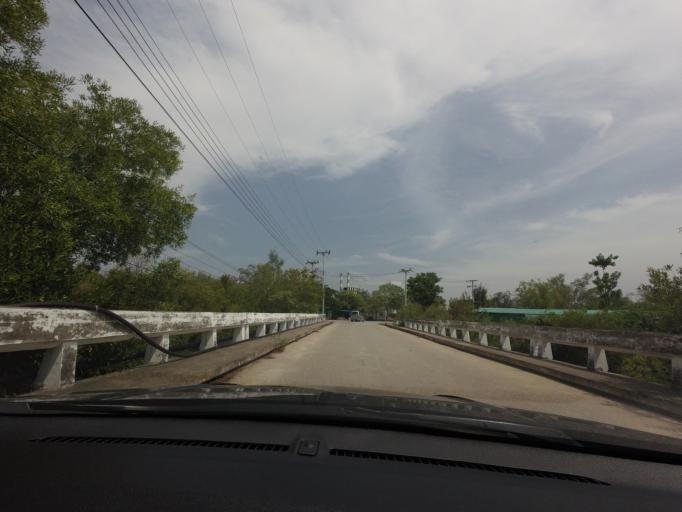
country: TH
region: Phetchaburi
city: Cha-am
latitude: 12.6878
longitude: 99.9603
